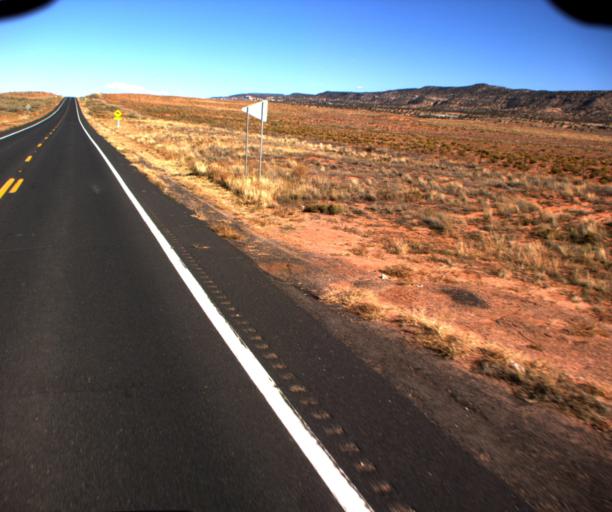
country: US
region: Arizona
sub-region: Coconino County
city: Kaibito
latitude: 36.3927
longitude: -110.8768
